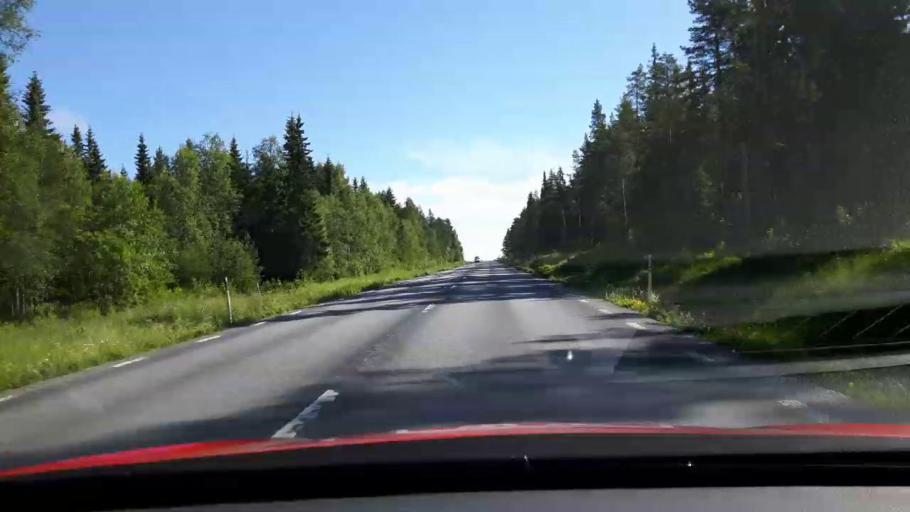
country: SE
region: Jaemtland
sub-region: OEstersunds Kommun
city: Lit
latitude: 63.2314
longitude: 14.7605
